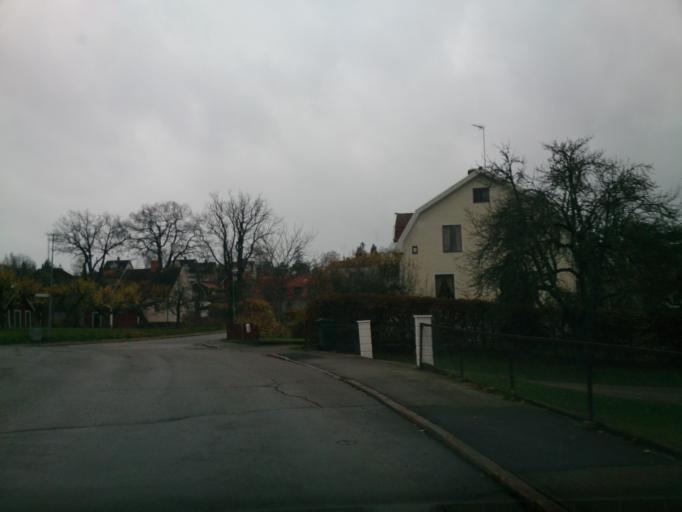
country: SE
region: OEstergoetland
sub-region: Atvidabergs Kommun
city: Atvidaberg
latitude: 58.2048
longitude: 15.9936
